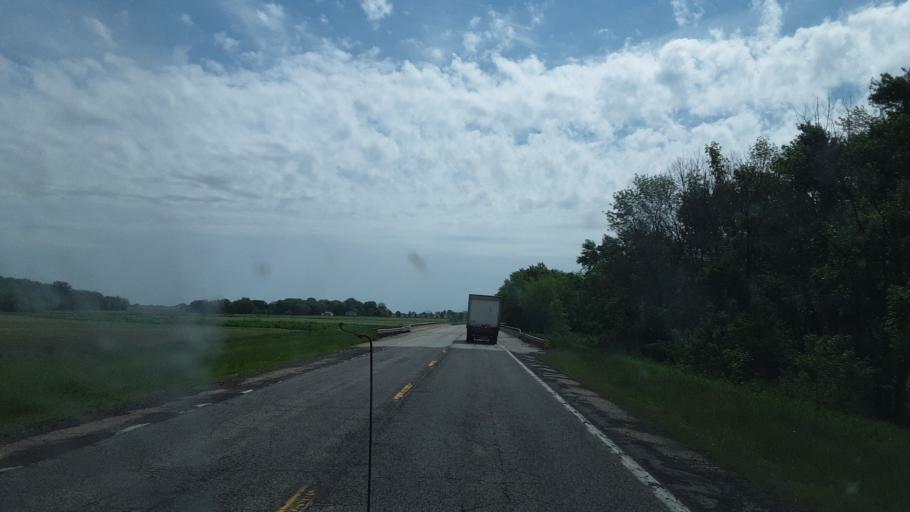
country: US
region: Illinois
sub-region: Logan County
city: Atlanta
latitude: 40.3104
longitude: -89.2866
